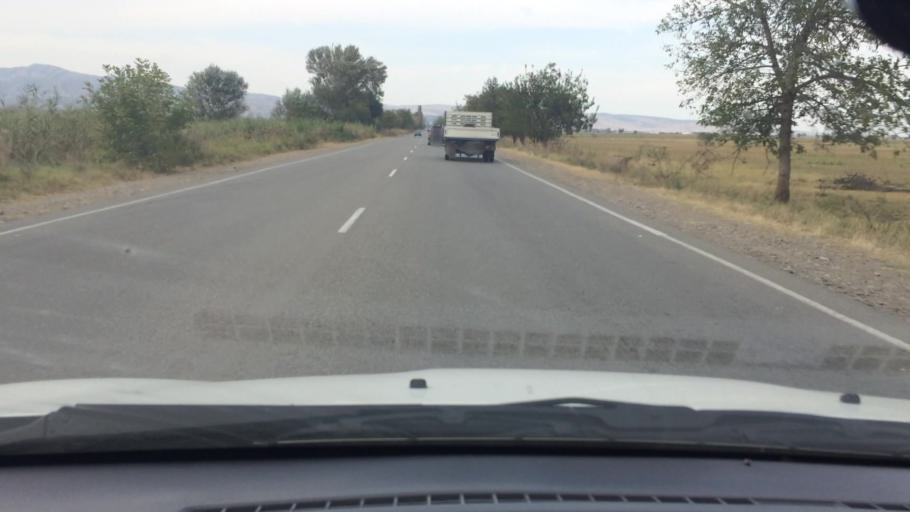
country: GE
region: Kvemo Kartli
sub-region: Marneuli
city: Marneuli
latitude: 41.5453
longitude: 44.7766
